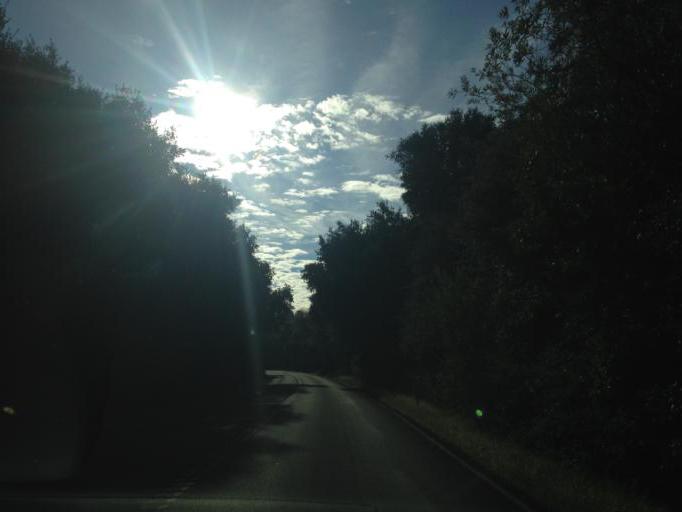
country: US
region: California
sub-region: San Diego County
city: Julian
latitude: 33.2091
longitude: -116.7316
